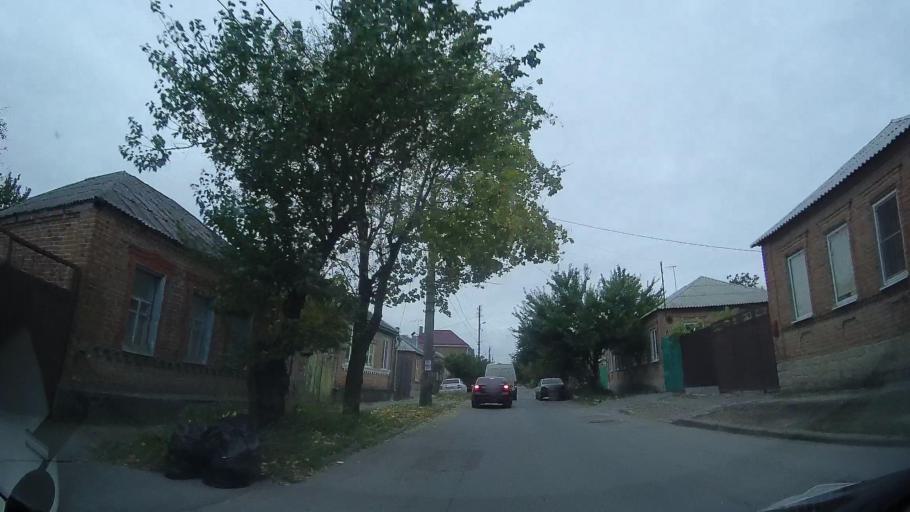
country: RU
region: Rostov
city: Severnyy
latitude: 47.2693
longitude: 39.6789
